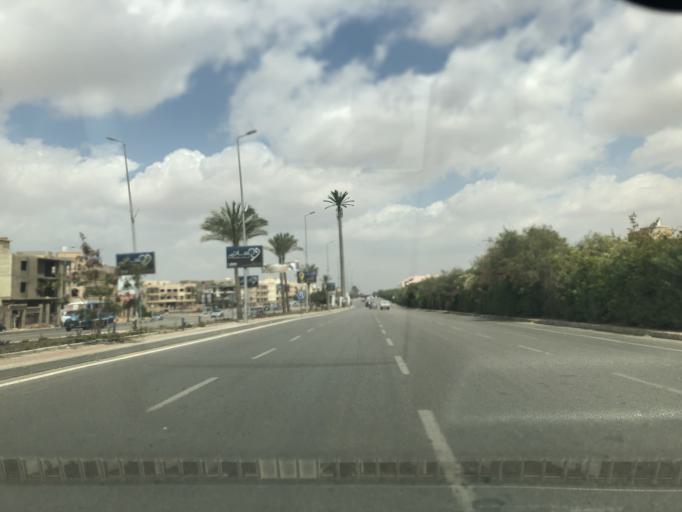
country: EG
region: Muhafazat al Qalyubiyah
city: Al Khankah
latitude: 30.0573
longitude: 31.4751
